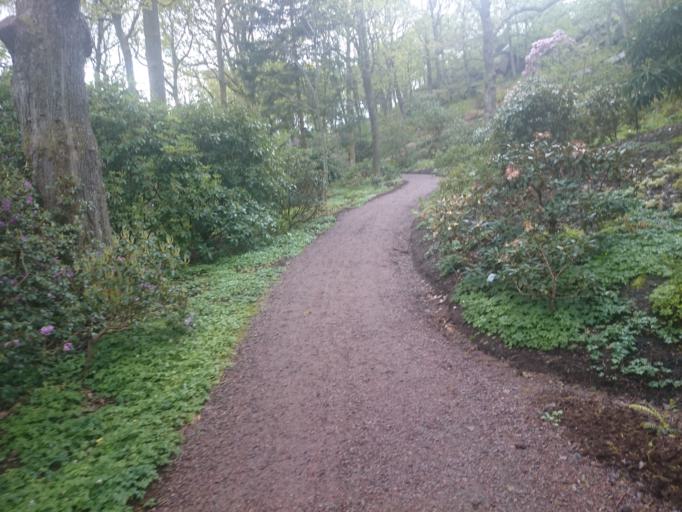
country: SE
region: Vaestra Goetaland
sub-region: Goteborg
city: Goeteborg
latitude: 57.6800
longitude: 11.9536
